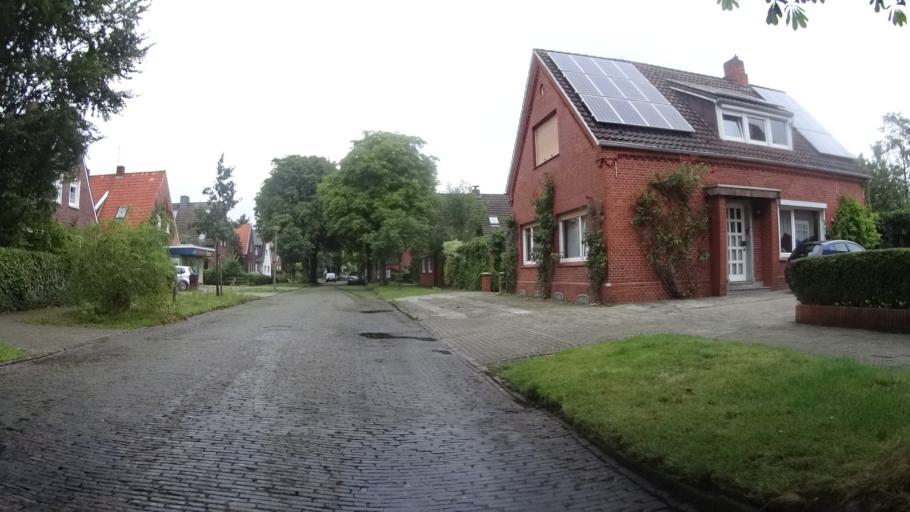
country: DE
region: Lower Saxony
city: Leer
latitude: 53.2334
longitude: 7.4452
